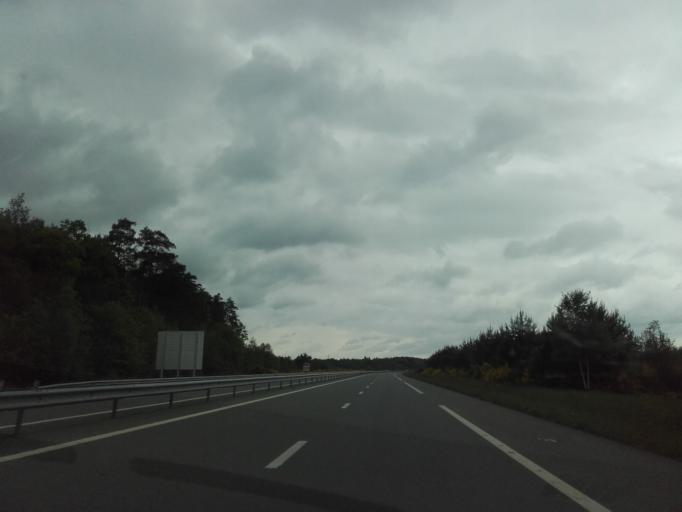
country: FR
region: Limousin
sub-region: Departement de la Correze
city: Correze
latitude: 45.3277
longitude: 1.8912
